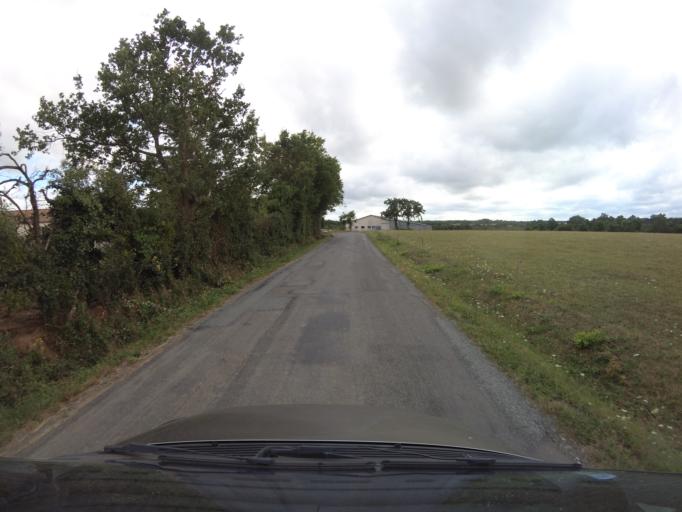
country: FR
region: Pays de la Loire
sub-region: Departement de la Vendee
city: Saint-Philbert-de-Bouaine
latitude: 47.0151
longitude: -1.5504
